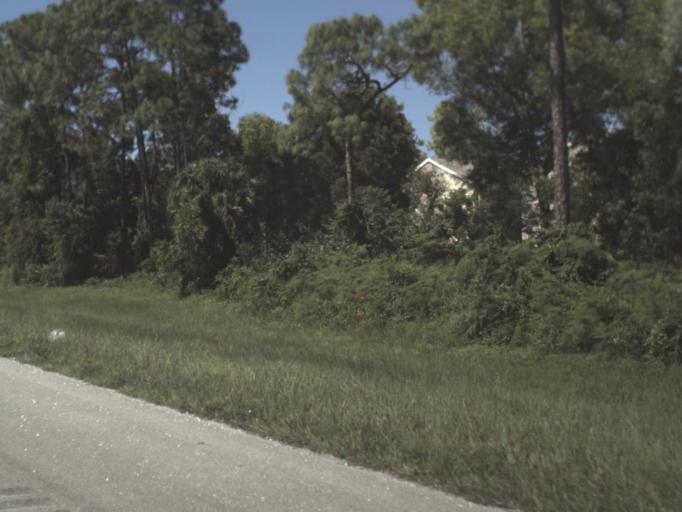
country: US
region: Florida
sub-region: Collier County
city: Golden Gate
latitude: 26.1645
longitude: -81.7139
